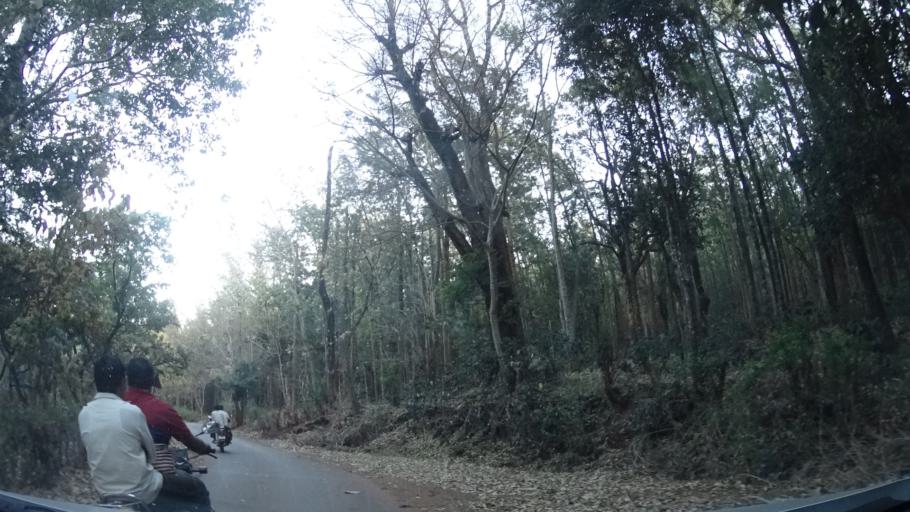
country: IN
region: Karnataka
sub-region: Chikmagalur
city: Tarikere
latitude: 13.5649
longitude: 75.7681
